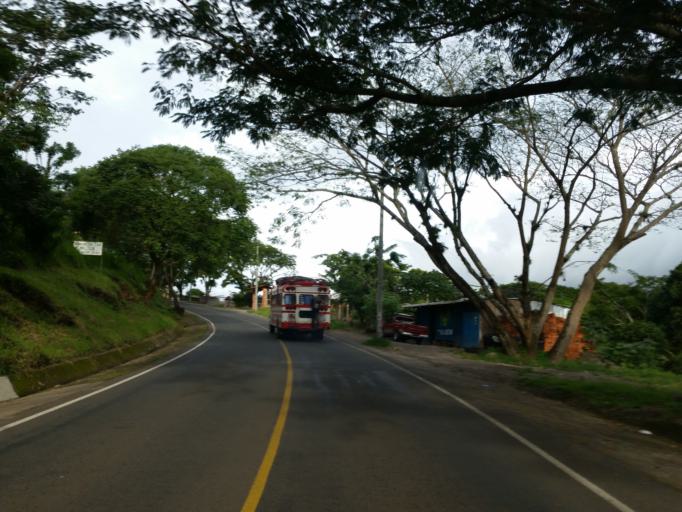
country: NI
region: Matagalpa
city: Matagalpa
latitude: 12.9403
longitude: -85.9004
